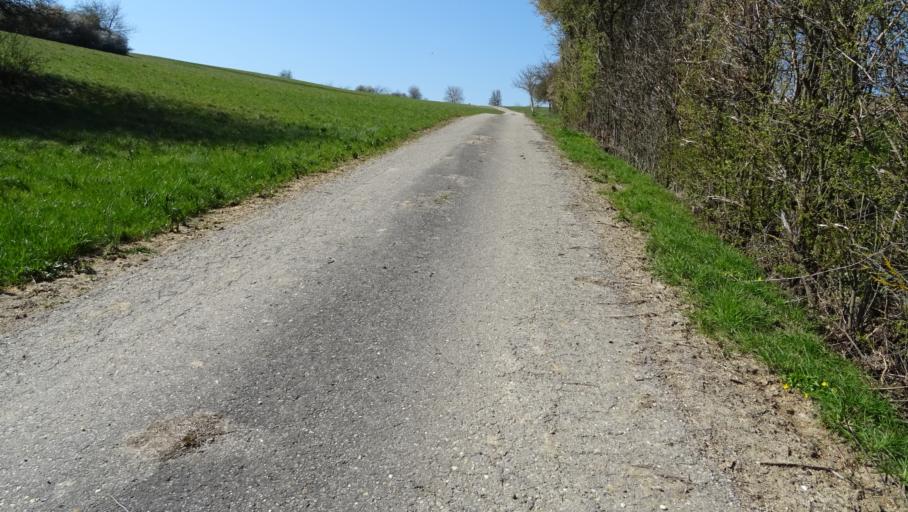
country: DE
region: Baden-Wuerttemberg
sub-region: Karlsruhe Region
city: Limbach
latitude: 49.4204
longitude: 9.2514
